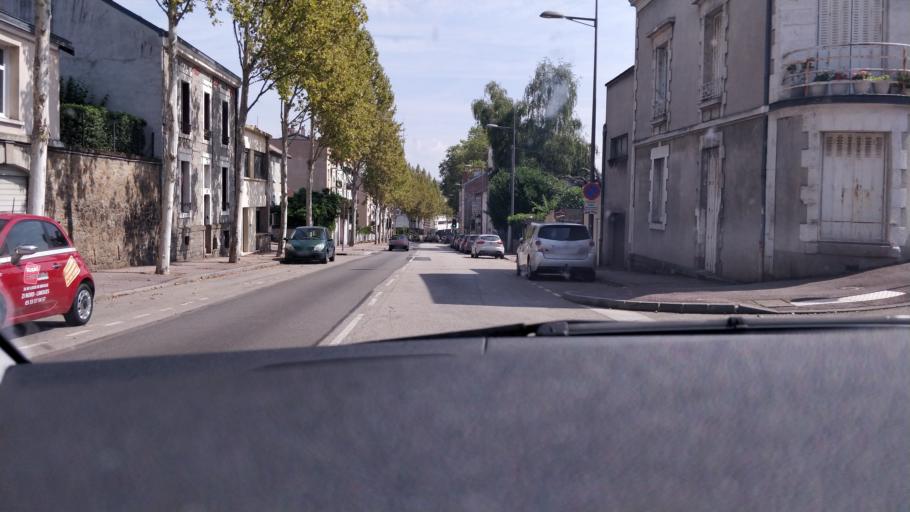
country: FR
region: Limousin
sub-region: Departement de la Haute-Vienne
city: Limoges
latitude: 45.8445
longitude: 1.2488
